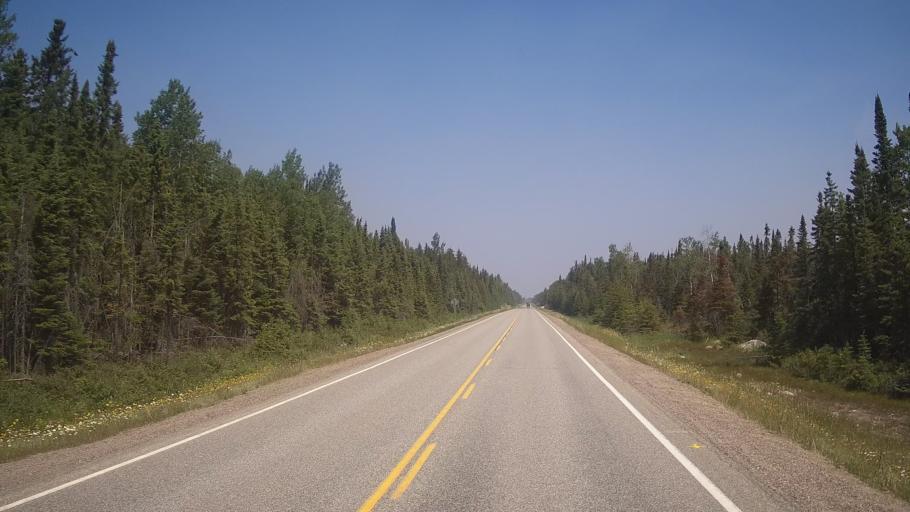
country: CA
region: Ontario
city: Timmins
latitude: 48.1008
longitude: -81.5911
